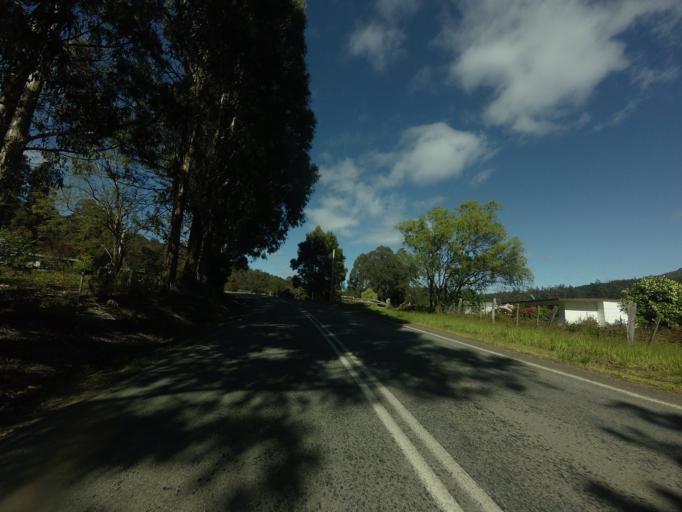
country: AU
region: Tasmania
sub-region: Derwent Valley
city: New Norfolk
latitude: -42.7247
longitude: 146.6758
